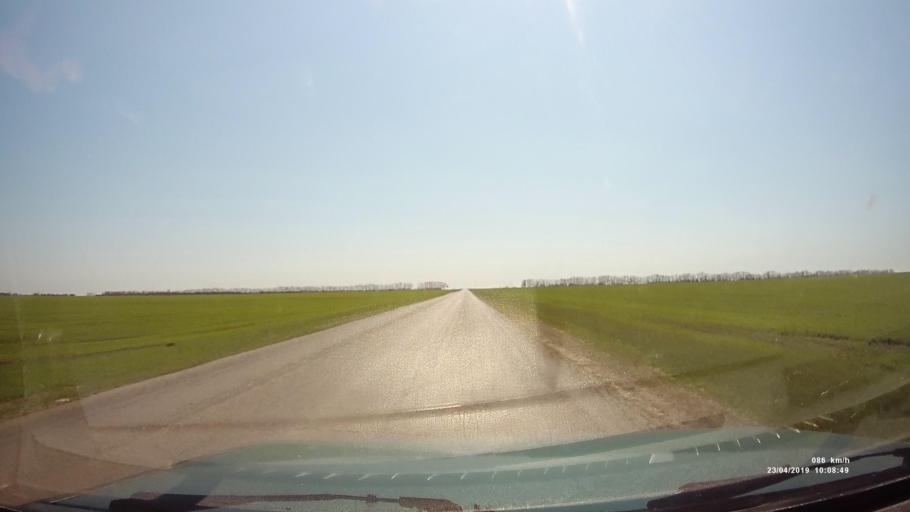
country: RU
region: Rostov
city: Sovetskoye
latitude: 46.7164
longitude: 42.2715
